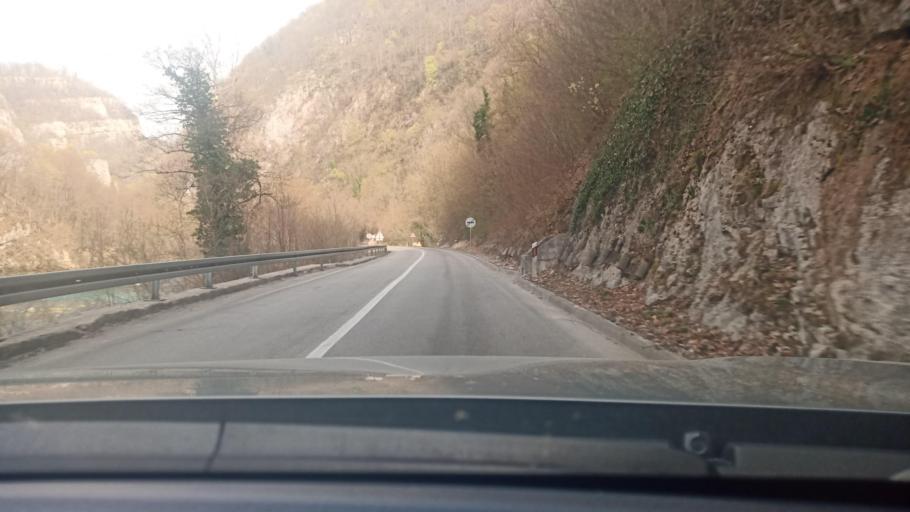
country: BA
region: Federation of Bosnia and Herzegovina
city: Bosanska Krupa
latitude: 44.8647
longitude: 16.0928
